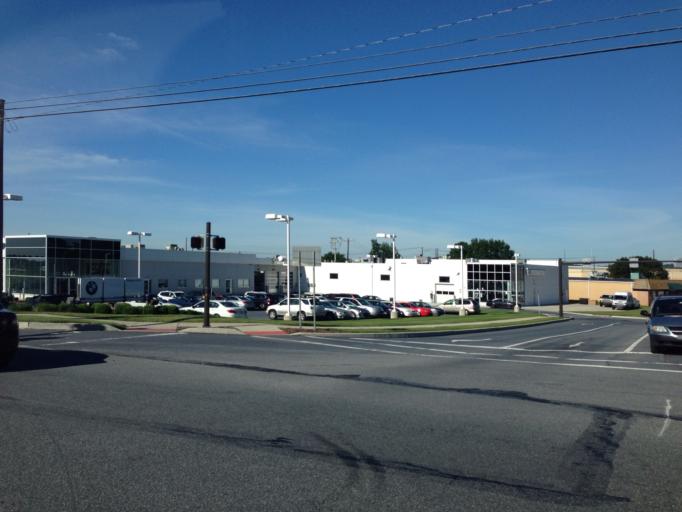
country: US
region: Pennsylvania
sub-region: Lancaster County
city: East Petersburg
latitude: 40.0786
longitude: -76.3385
